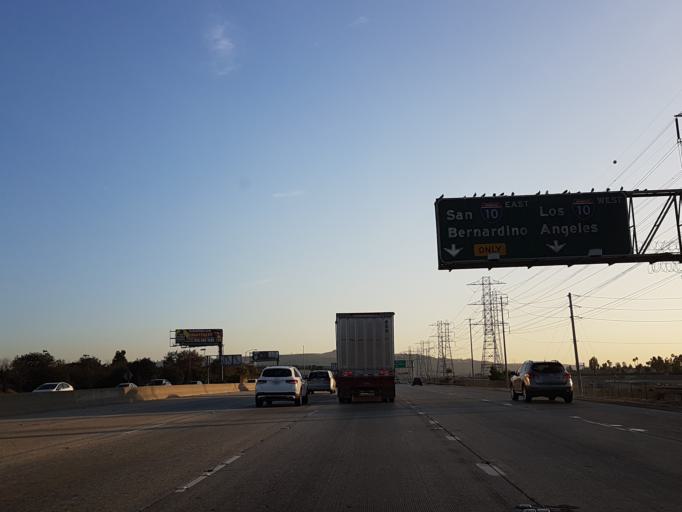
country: US
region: California
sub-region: Los Angeles County
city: El Monte
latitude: 34.0732
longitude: -117.9994
